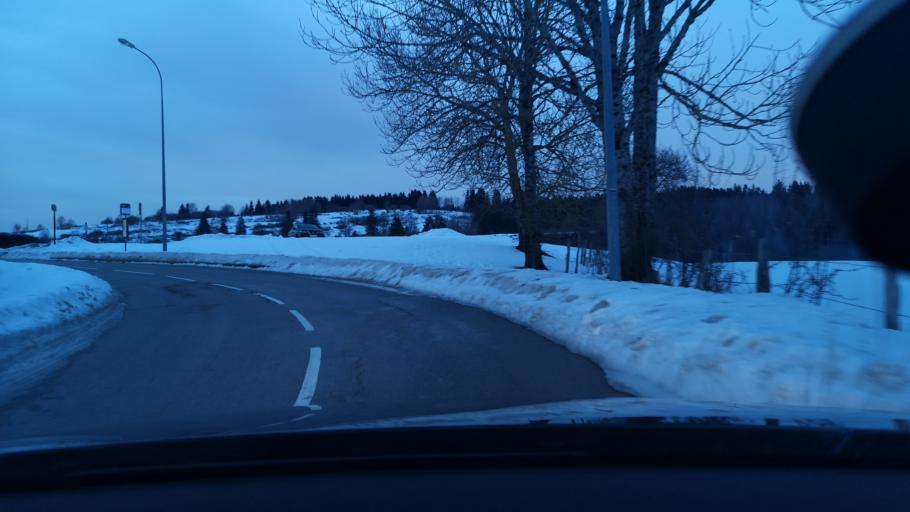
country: FR
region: Franche-Comte
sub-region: Departement du Doubs
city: Pontarlier
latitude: 46.9042
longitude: 6.3715
